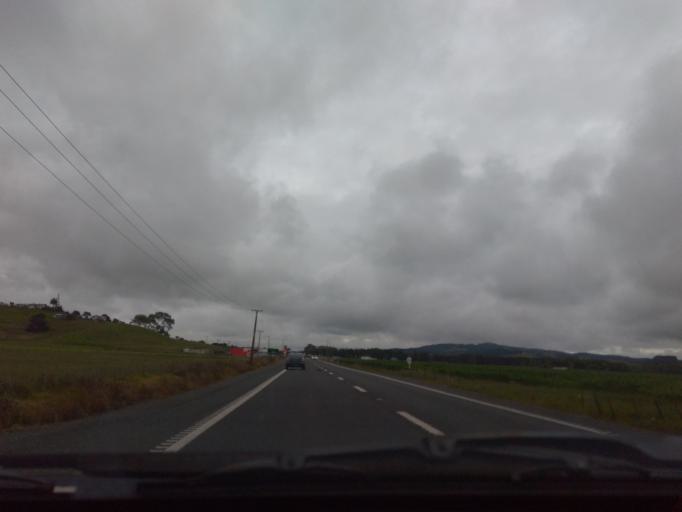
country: NZ
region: Northland
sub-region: Whangarei
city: Ruakaka
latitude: -35.8950
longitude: 174.4373
